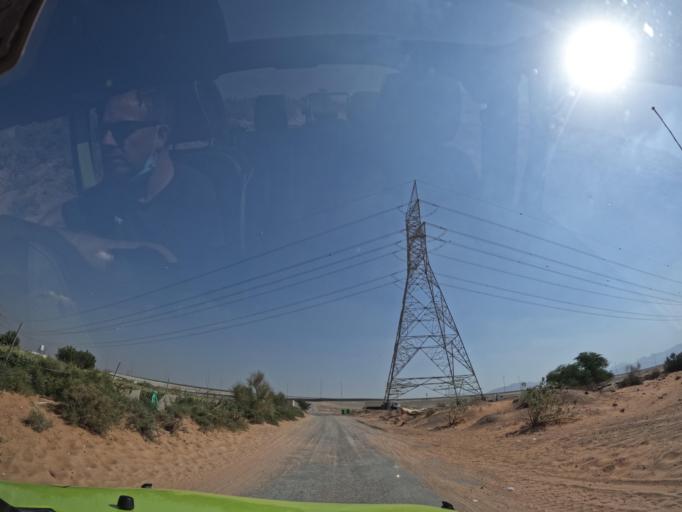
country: AE
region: Ash Shariqah
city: Adh Dhayd
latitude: 24.8009
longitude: 55.7991
